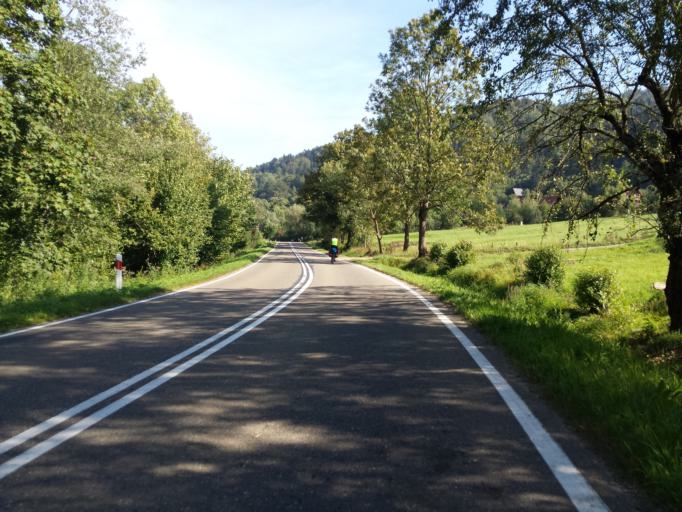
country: PL
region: Subcarpathian Voivodeship
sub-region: Powiat leski
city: Baligrod
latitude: 49.3078
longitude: 22.2767
